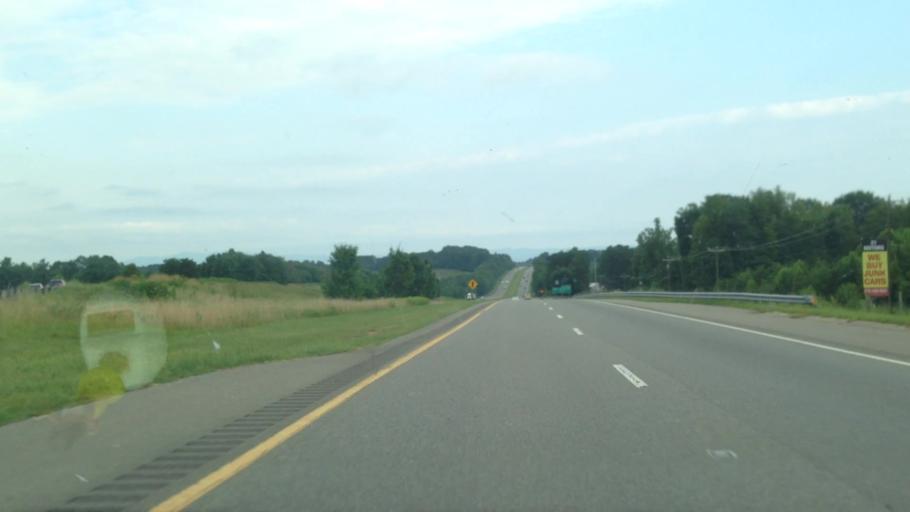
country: US
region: North Carolina
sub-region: Surry County
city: Flat Rock
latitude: 36.4463
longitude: -80.5451
